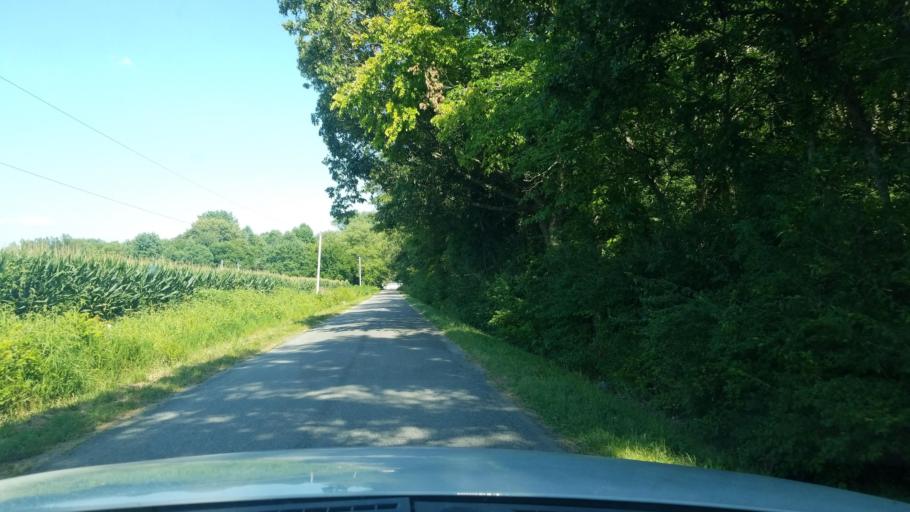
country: US
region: Illinois
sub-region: Saline County
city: Eldorado
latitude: 37.8050
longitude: -88.4629
